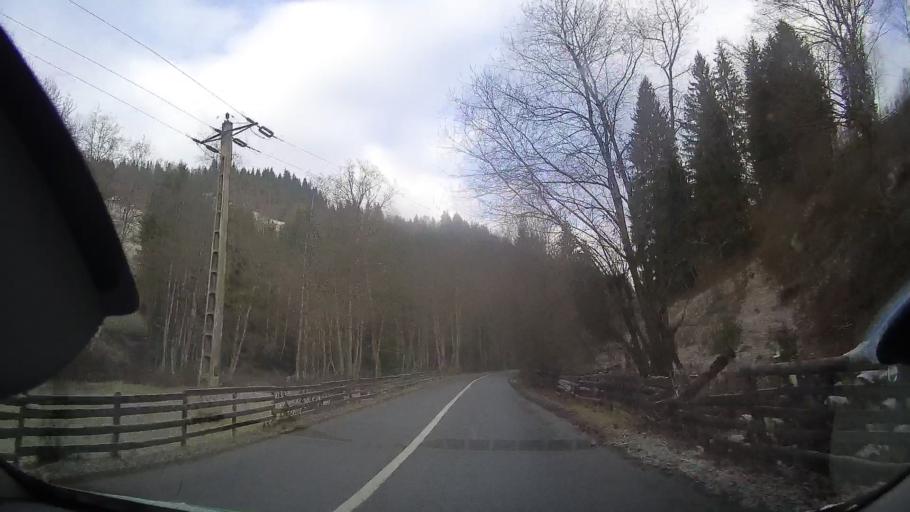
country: RO
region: Alba
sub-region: Comuna Horea
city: Horea
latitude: 46.4812
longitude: 22.9613
